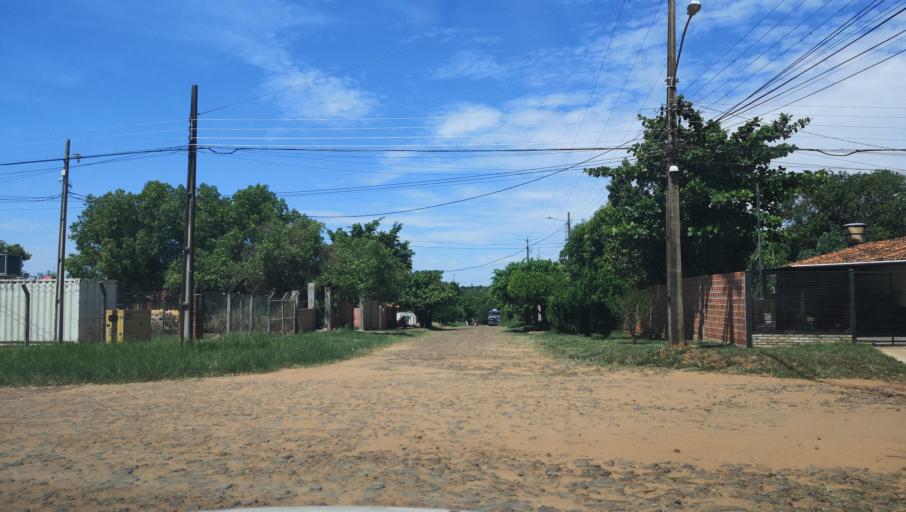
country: PY
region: Misiones
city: Santa Maria
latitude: -26.8803
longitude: -57.0290
